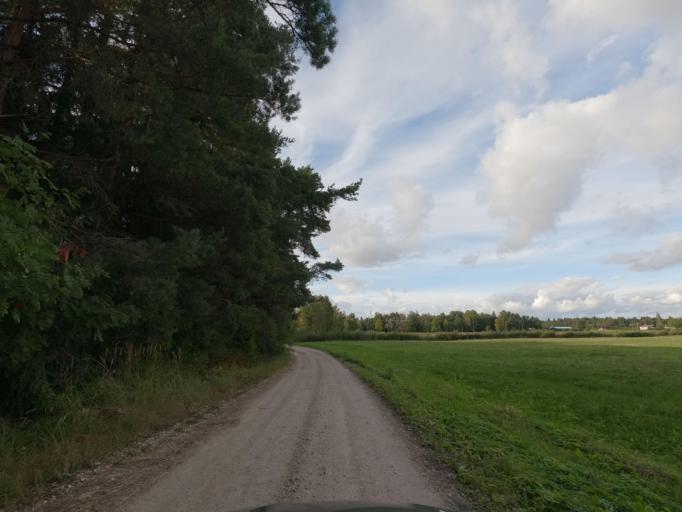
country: EE
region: Raplamaa
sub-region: Rapla vald
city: Rapla
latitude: 59.0170
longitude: 24.7669
